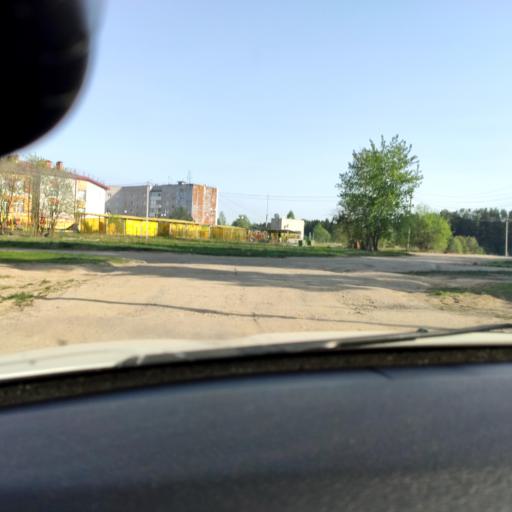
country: RU
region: Perm
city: Polazna
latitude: 58.2962
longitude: 56.3880
